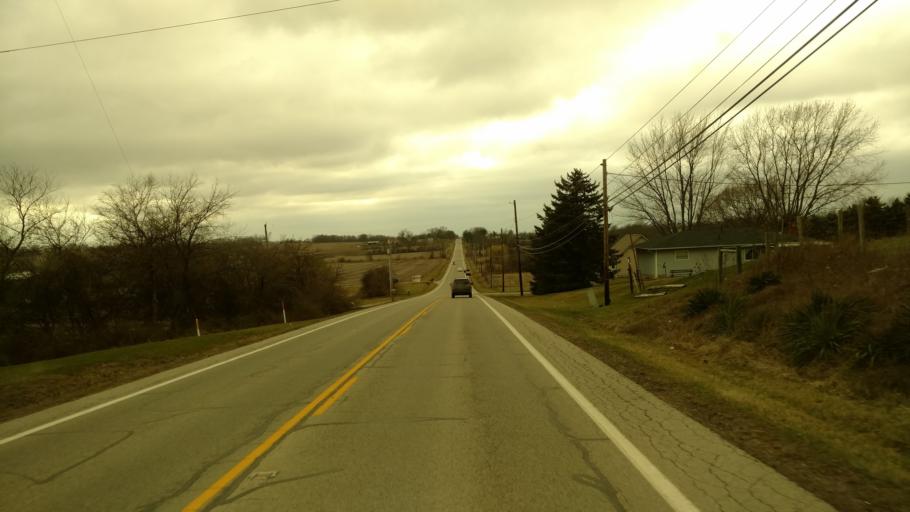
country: US
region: Ohio
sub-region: Perry County
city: Thornport
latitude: 39.9586
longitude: -82.3898
